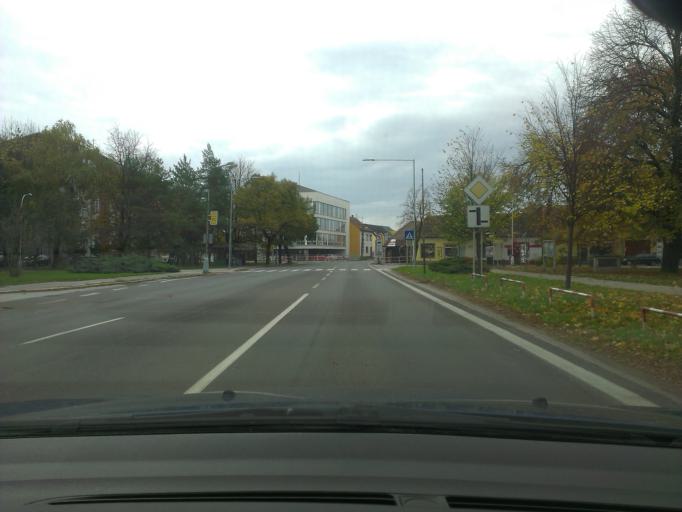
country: SK
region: Trnavsky
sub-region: Okres Trnava
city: Piestany
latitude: 48.5946
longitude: 17.8240
